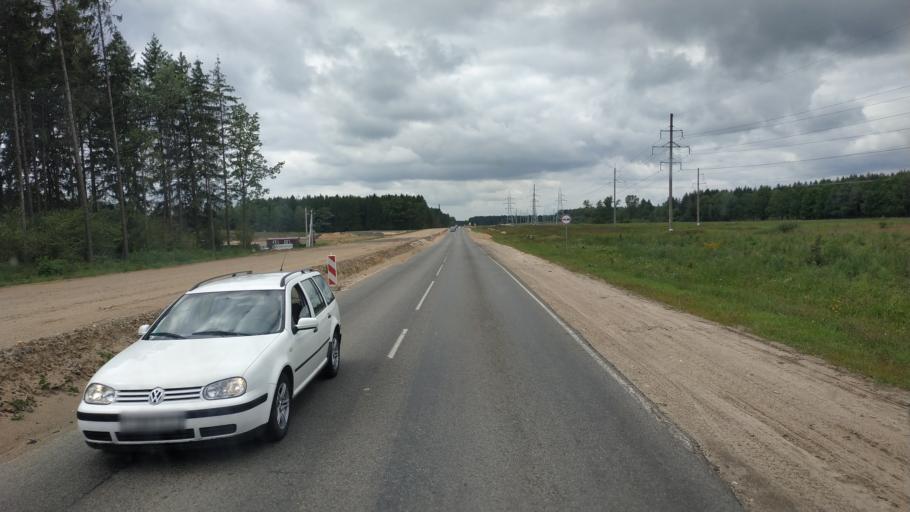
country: BY
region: Mogilev
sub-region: Mahilyowski Rayon
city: Kadino
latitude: 53.8722
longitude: 30.4508
